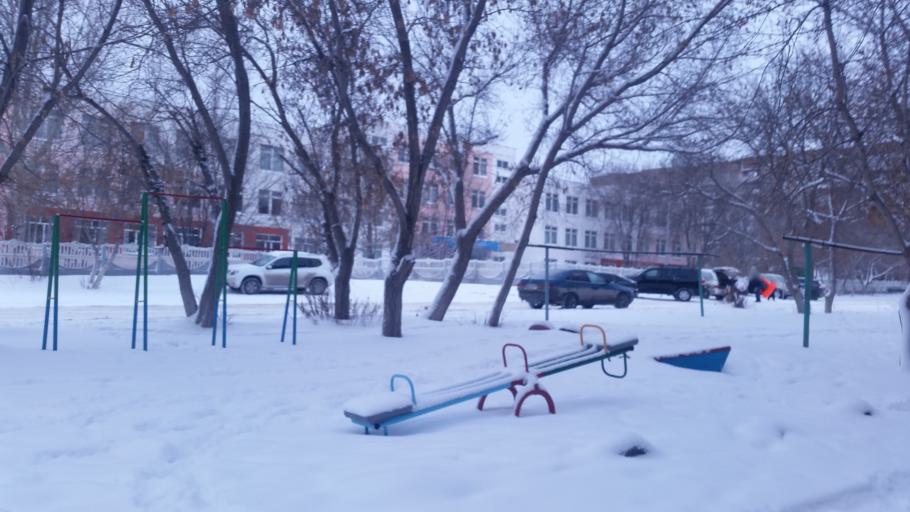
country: KZ
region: Qaraghandy
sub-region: Qaraghandy Qalasy
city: Karagandy
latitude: 49.7720
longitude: 73.1531
